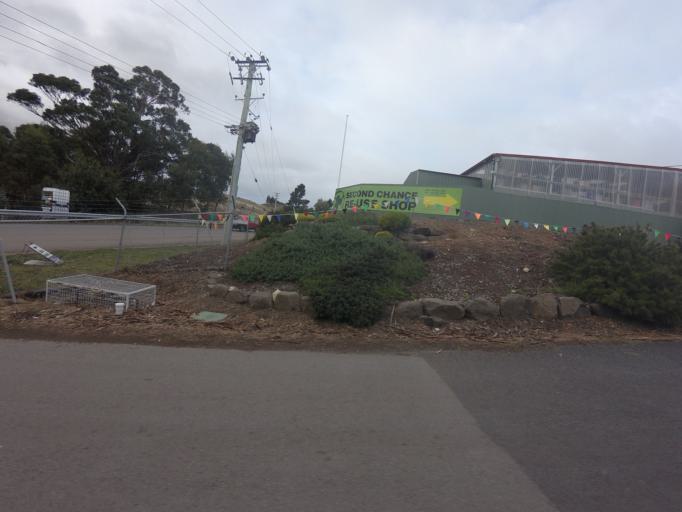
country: AU
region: Tasmania
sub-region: Clarence
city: Warrane
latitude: -42.8616
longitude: 147.4074
